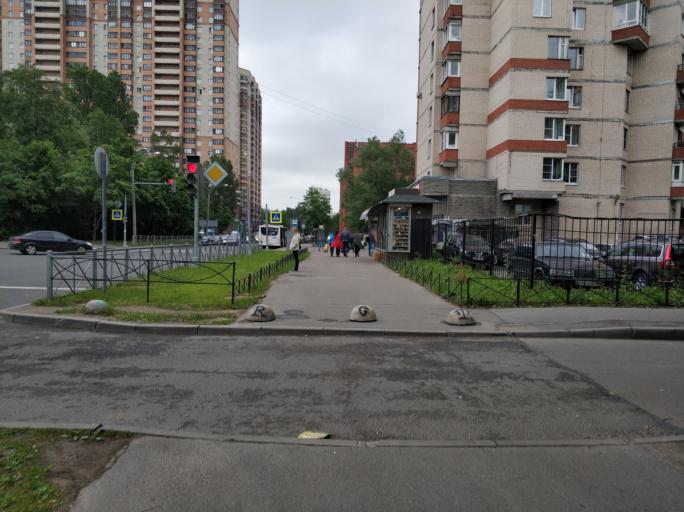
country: RU
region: St.-Petersburg
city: Grazhdanka
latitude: 60.0327
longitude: 30.4005
